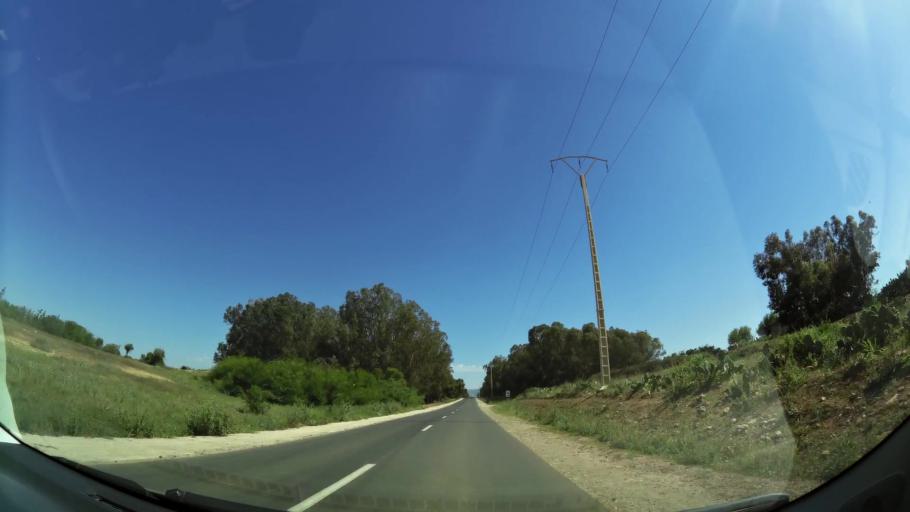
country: MA
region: Oriental
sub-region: Berkane-Taourirt
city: Madagh
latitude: 35.0060
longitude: -2.3982
